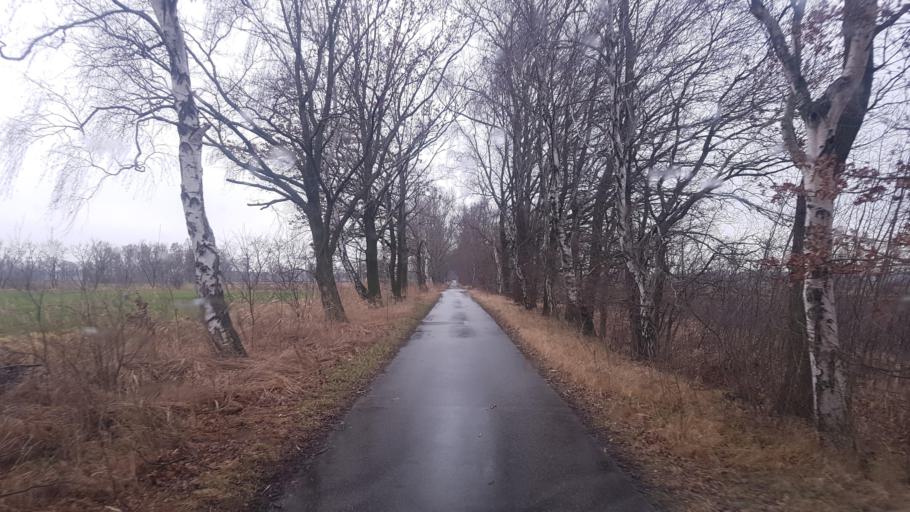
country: DE
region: Brandenburg
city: Grossthiemig
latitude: 51.4137
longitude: 13.6494
